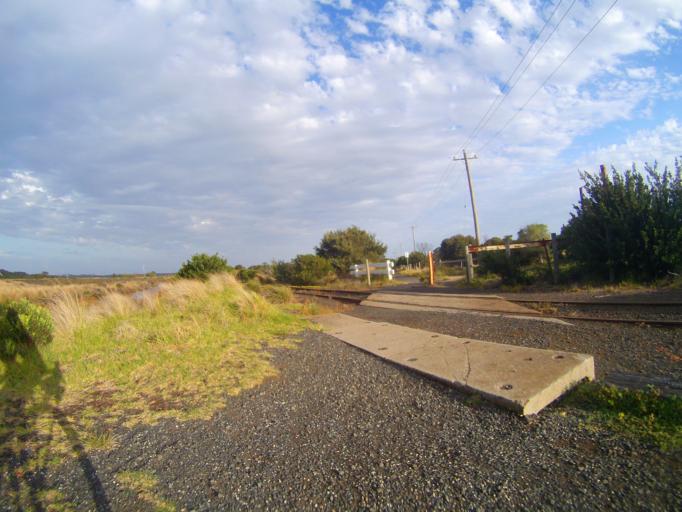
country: AU
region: Victoria
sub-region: Queenscliffe
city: Queenscliff
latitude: -38.2626
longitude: 144.6169
